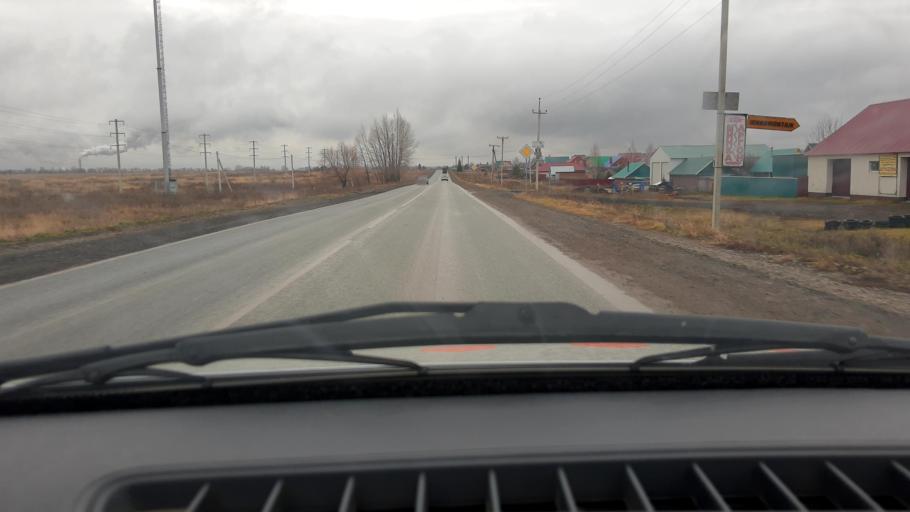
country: RU
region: Bashkortostan
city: Iglino
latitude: 54.7862
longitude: 56.2526
